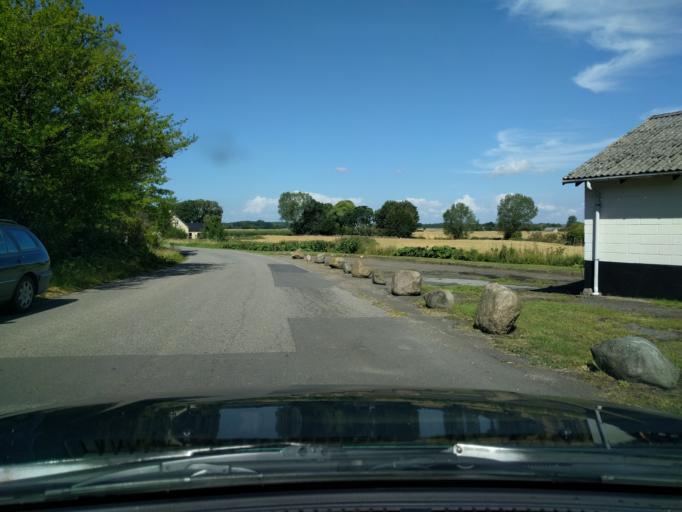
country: DK
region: Zealand
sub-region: Vordingborg Kommune
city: Orslev
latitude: 55.0984
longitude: 11.9262
